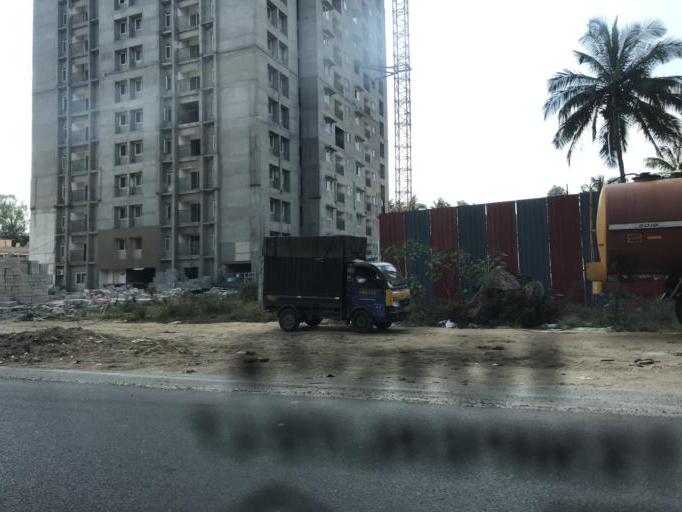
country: IN
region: Karnataka
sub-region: Bangalore Urban
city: Bangalore
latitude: 12.8434
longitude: 77.5882
